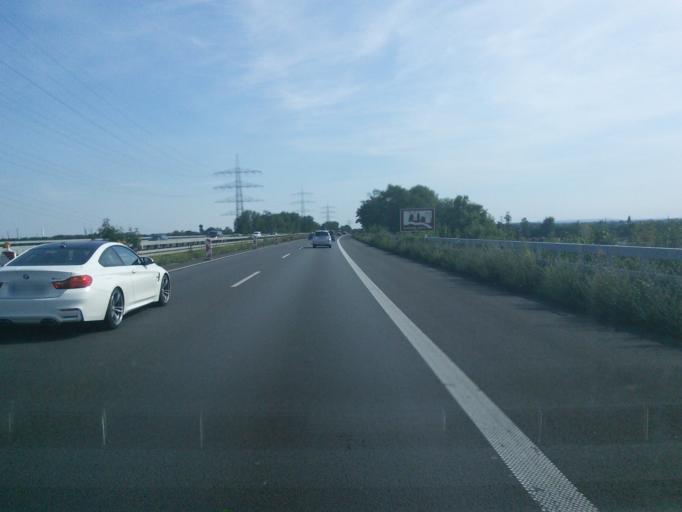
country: DE
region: North Rhine-Westphalia
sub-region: Regierungsbezirk Dusseldorf
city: Dormagen
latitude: 51.1150
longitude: 6.7999
